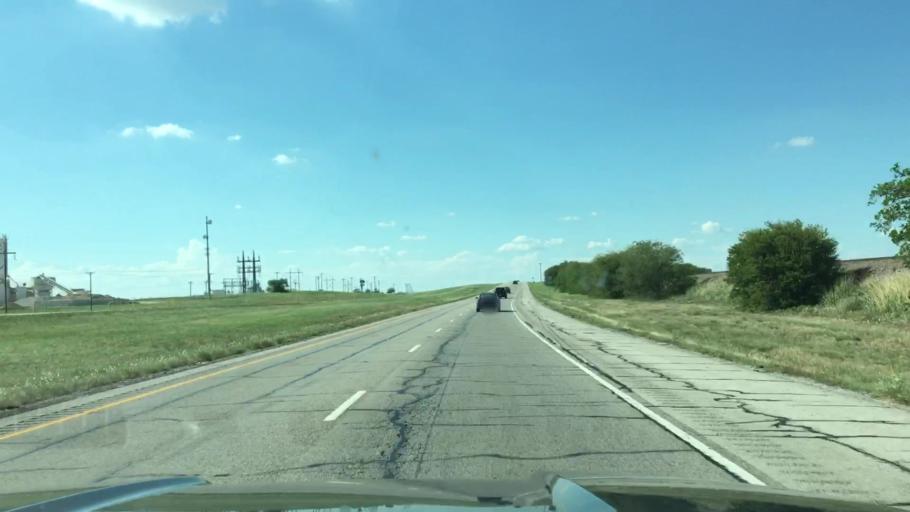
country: US
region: Texas
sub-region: Wise County
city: Decatur
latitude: 33.1759
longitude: -97.5434
